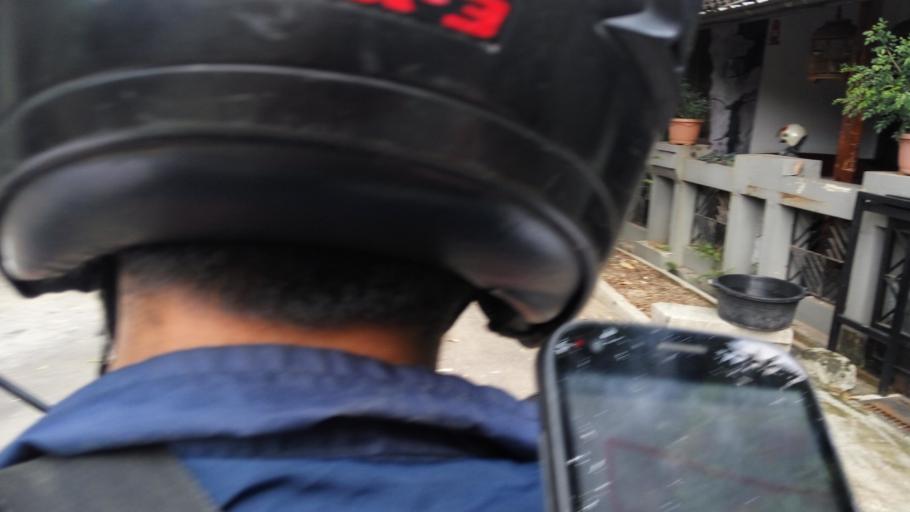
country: ID
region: Central Java
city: Mranggen
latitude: -7.0367
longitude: 110.4695
